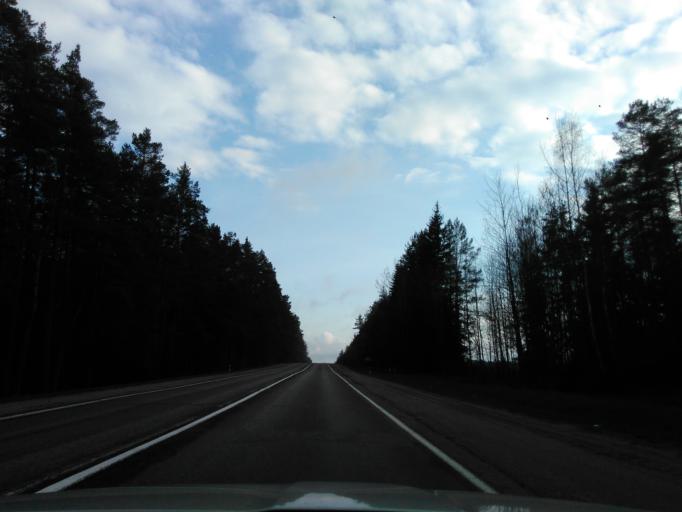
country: BY
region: Minsk
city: Lahoysk
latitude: 54.2653
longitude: 27.8562
